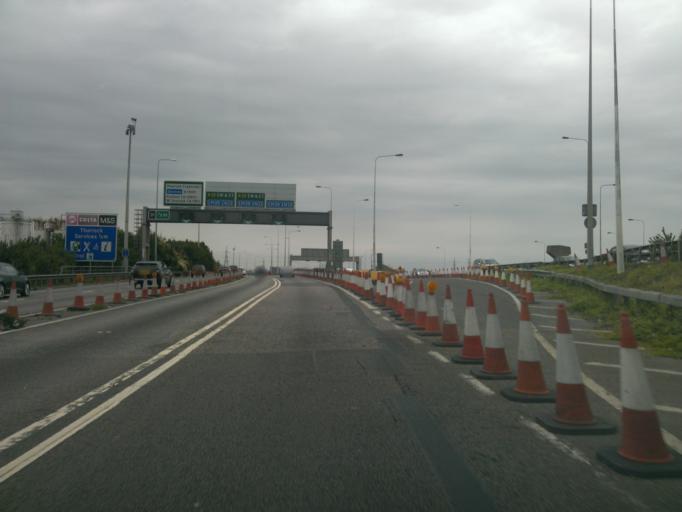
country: GB
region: England
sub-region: Kent
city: West Thurrock
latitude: 51.4770
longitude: 0.2664
